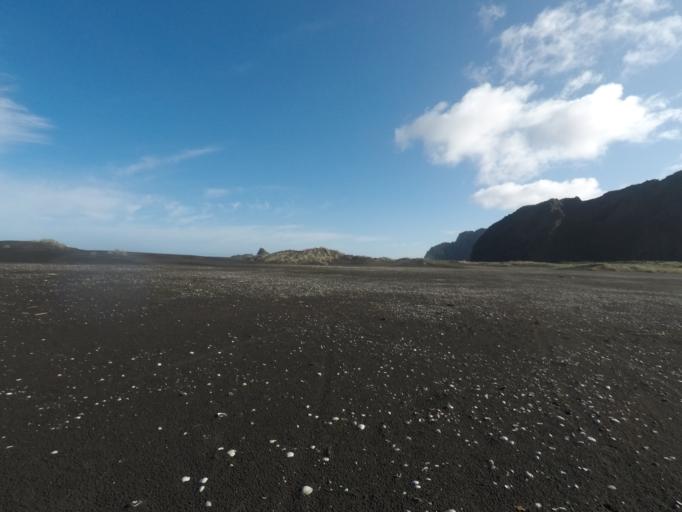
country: NZ
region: Auckland
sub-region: Auckland
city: Muriwai Beach
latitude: -36.9980
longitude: 174.4751
